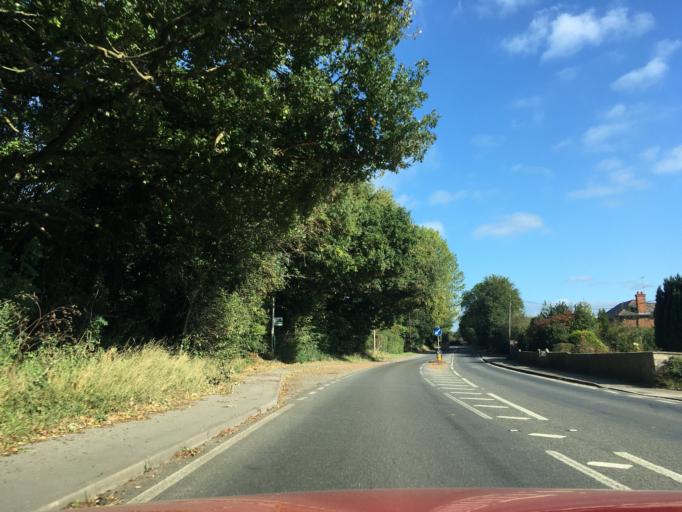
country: GB
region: England
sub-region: Hampshire
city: Tadley
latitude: 51.3960
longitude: -1.1657
